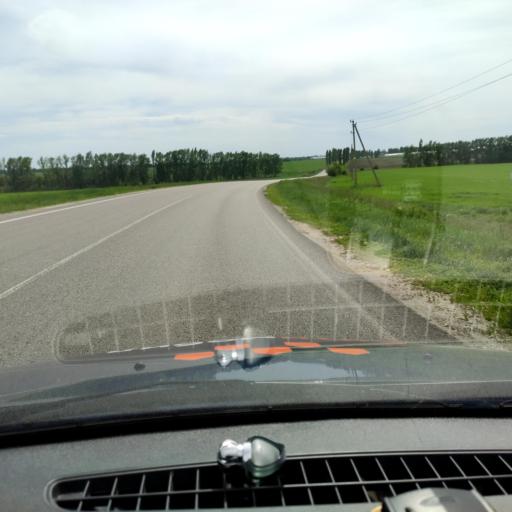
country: RU
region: Voronezj
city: Novaya Usman'
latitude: 51.5552
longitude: 39.3753
